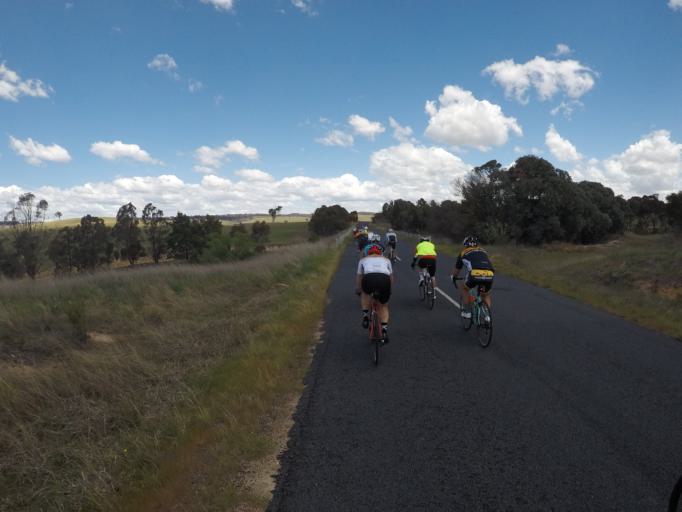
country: AU
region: New South Wales
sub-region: Bathurst Regional
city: Perthville
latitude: -33.5643
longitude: 149.4160
